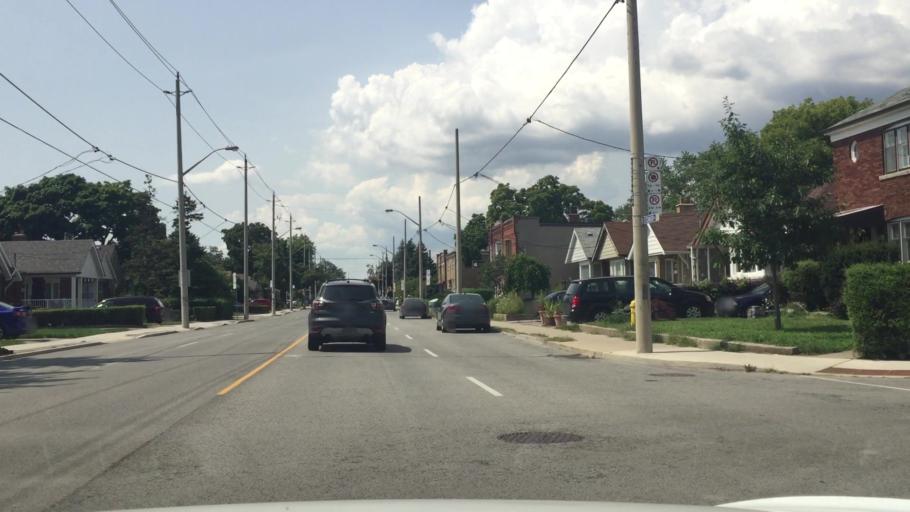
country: CA
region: Ontario
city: Toronto
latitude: 43.6941
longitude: -79.3461
